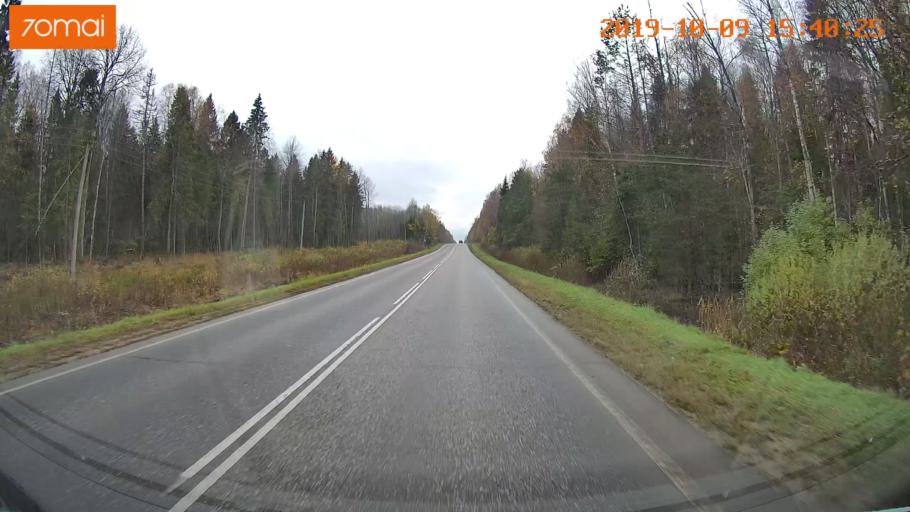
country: RU
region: Kostroma
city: Oktyabr'skiy
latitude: 57.8878
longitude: 41.1449
